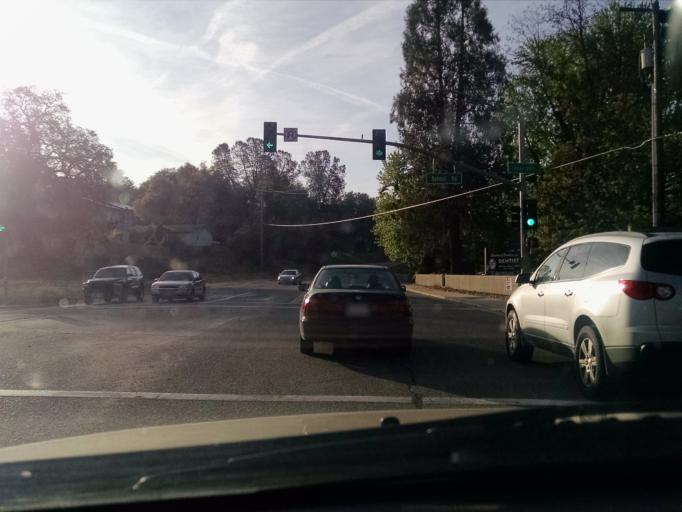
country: US
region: California
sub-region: Madera County
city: Oakhurst
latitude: 37.3279
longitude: -119.6477
